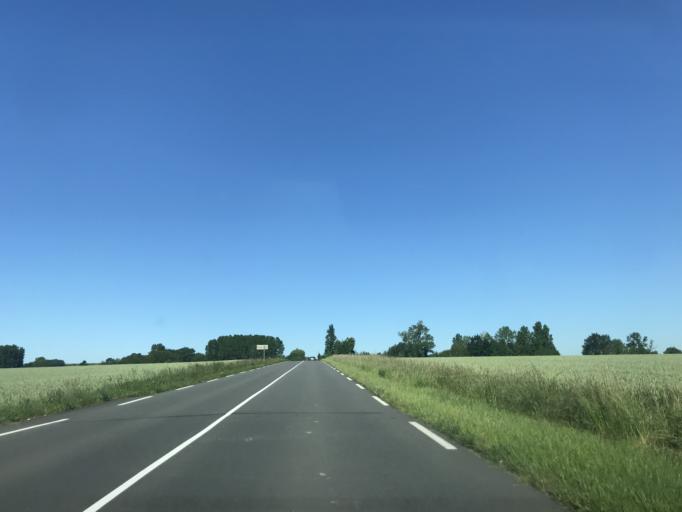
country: FR
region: Poitou-Charentes
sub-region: Departement de la Charente
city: Barbezieux-Saint-Hilaire
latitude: 45.4976
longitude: -0.2404
